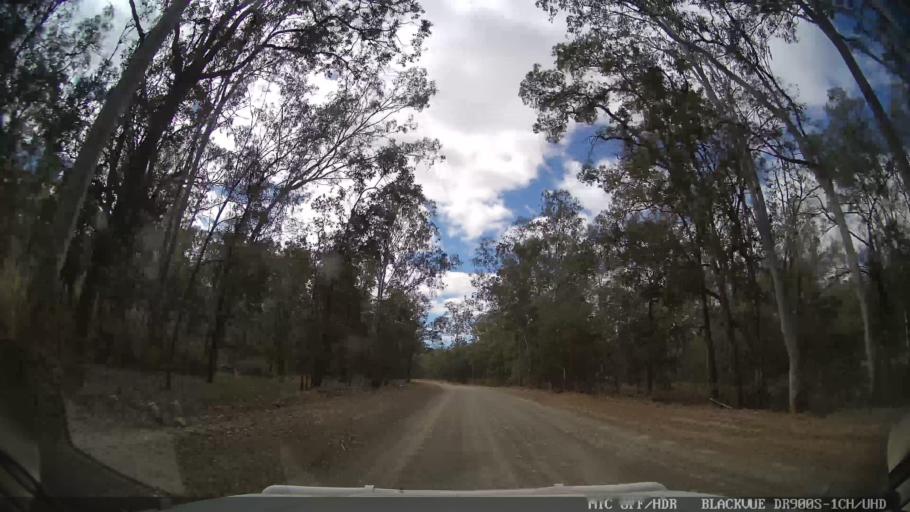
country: AU
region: Queensland
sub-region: Gladstone
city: Toolooa
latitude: -24.5500
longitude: 151.3419
